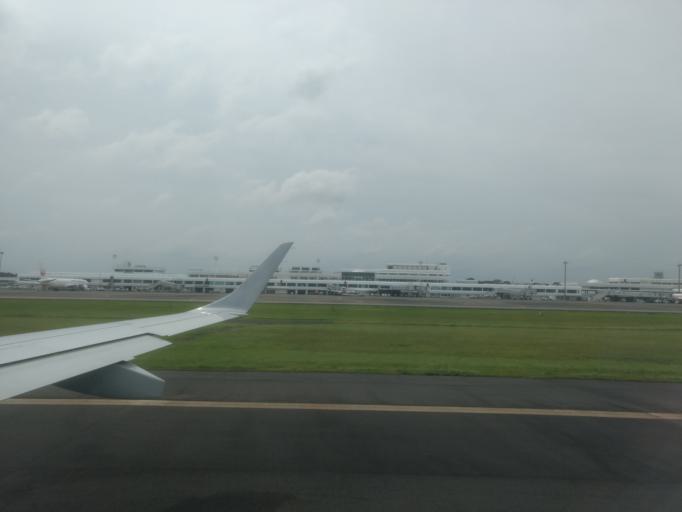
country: JP
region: Kagoshima
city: Kajiki
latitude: 31.8091
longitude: 130.7154
